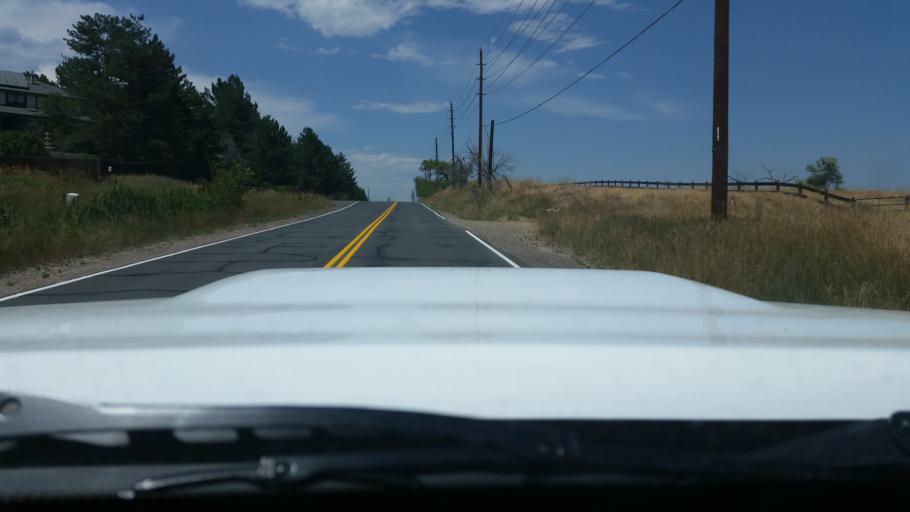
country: US
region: Colorado
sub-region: Broomfield County
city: Broomfield
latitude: 39.8937
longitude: -105.0811
